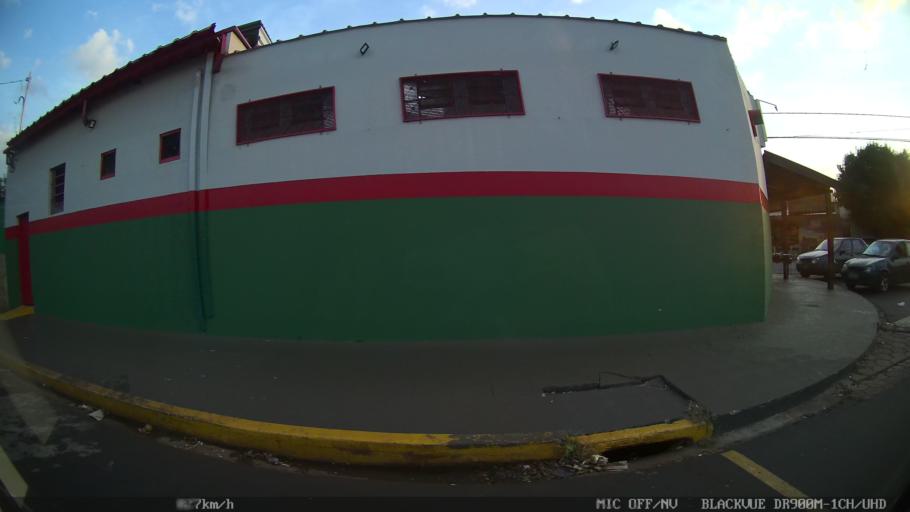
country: BR
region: Sao Paulo
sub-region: Ribeirao Preto
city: Ribeirao Preto
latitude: -21.1241
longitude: -47.8157
